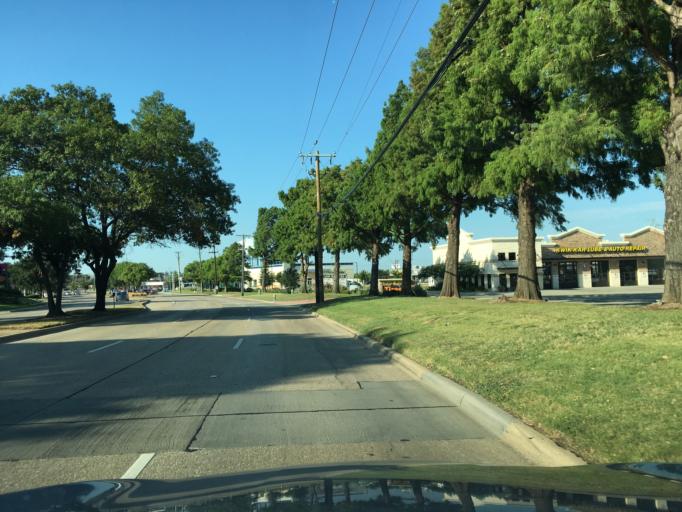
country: US
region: Texas
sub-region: Dallas County
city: Addison
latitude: 32.9553
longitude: -96.8554
